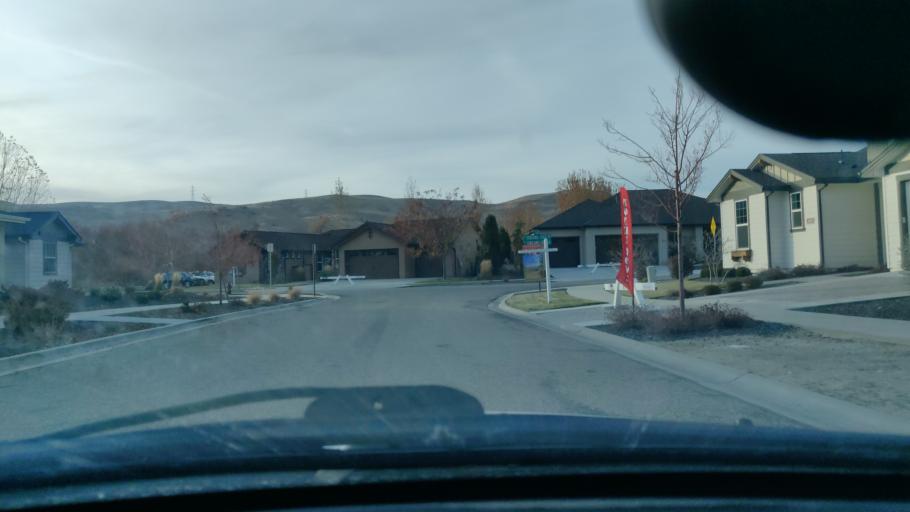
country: US
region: Idaho
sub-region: Ada County
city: Eagle
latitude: 43.7750
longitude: -116.2620
